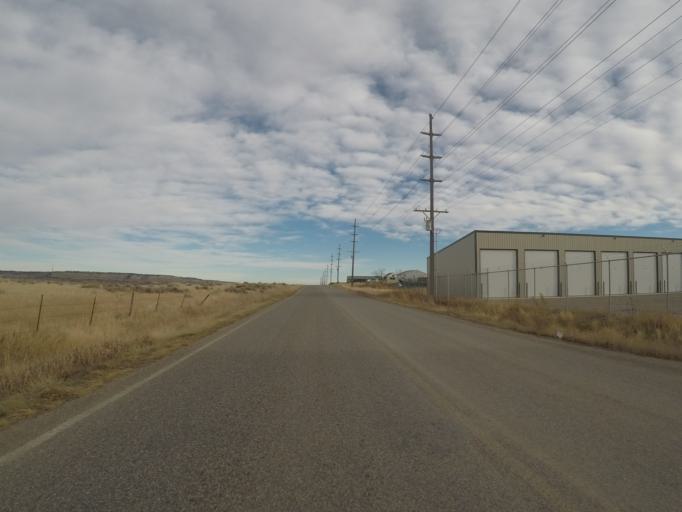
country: US
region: Montana
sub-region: Yellowstone County
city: Laurel
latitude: 45.7840
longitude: -108.7134
